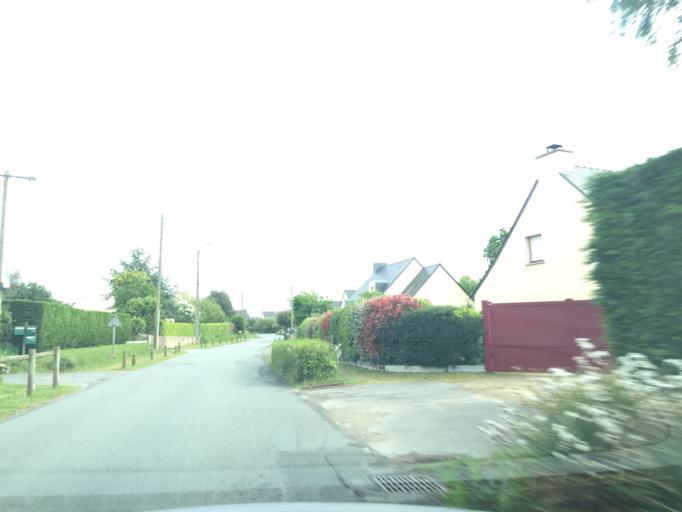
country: FR
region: Brittany
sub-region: Departement des Cotes-d'Armor
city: Crehen
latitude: 48.5793
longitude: -2.1968
